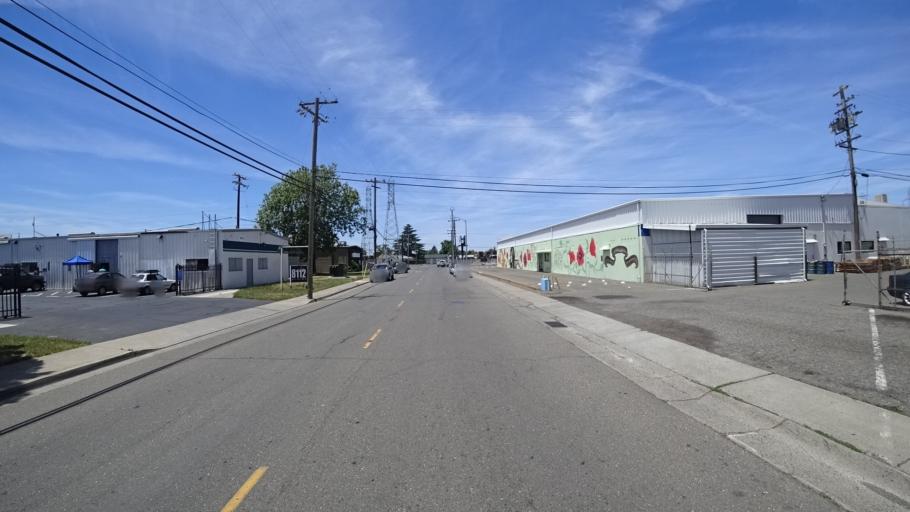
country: US
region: California
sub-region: Sacramento County
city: Florin
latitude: 38.5355
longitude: -121.4078
